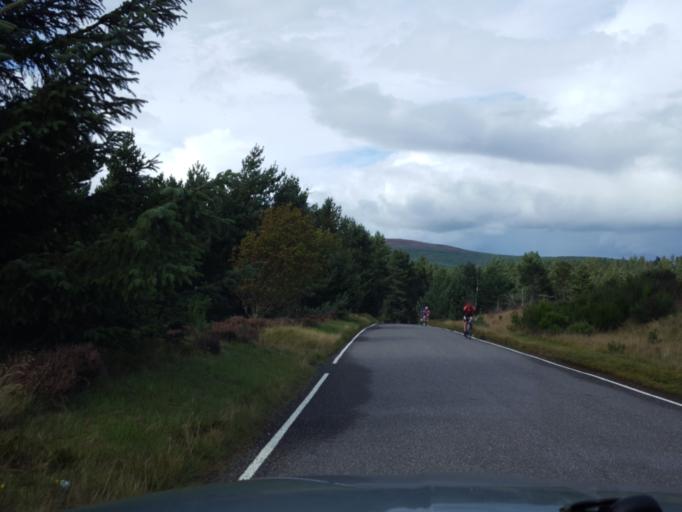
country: GB
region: Scotland
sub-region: Aberdeenshire
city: Banchory
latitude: 56.9454
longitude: -2.5783
